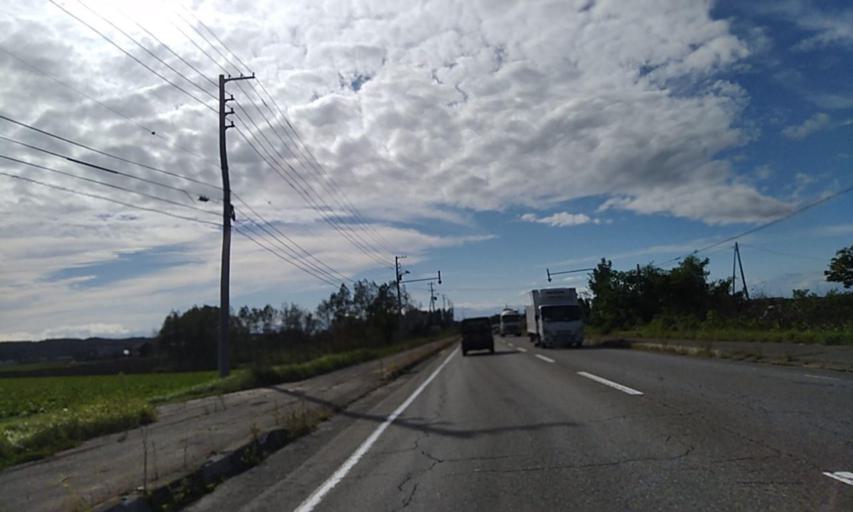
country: JP
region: Hokkaido
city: Obihiro
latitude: 42.9200
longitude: 143.3064
